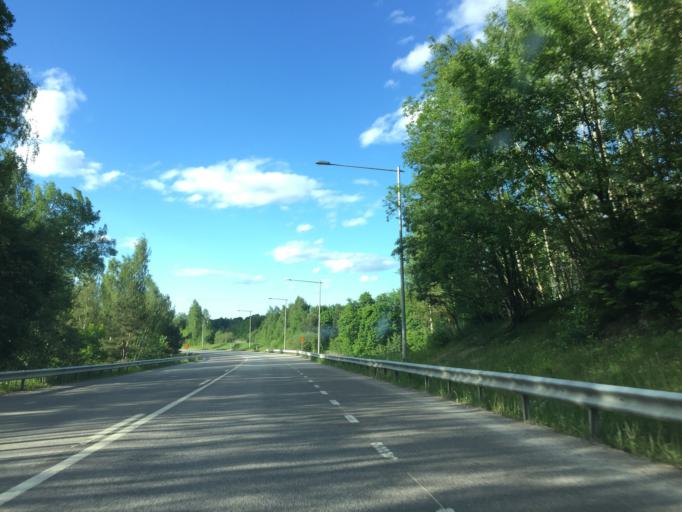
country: SE
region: OErebro
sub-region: Orebro Kommun
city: Orebro
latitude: 59.2489
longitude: 15.2383
